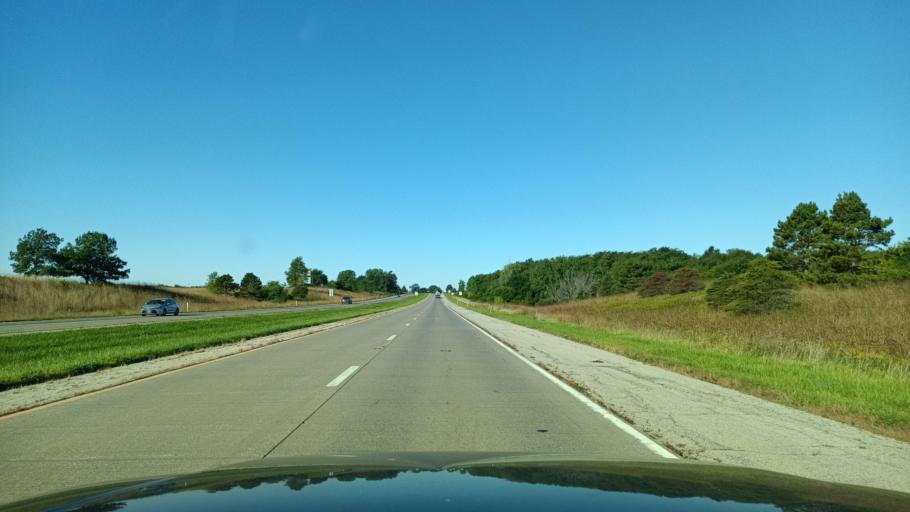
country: US
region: Illinois
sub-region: Warren County
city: Monmouth
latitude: 40.9258
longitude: -90.5979
